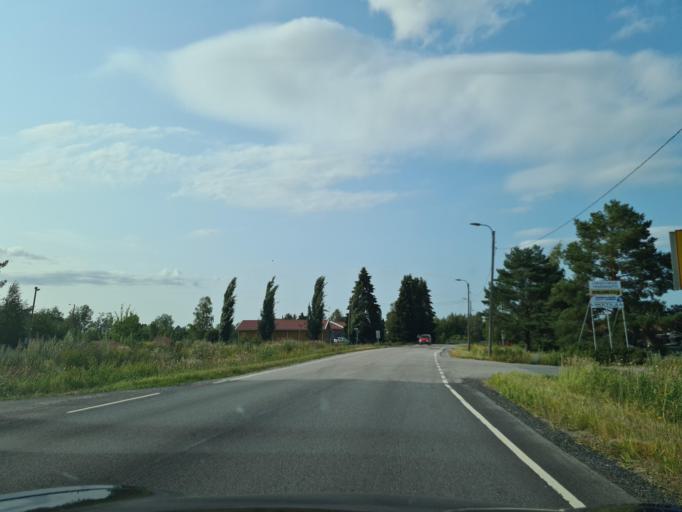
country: FI
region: Ostrobothnia
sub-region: Vaasa
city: Vaehaekyroe
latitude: 63.0066
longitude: 22.1499
